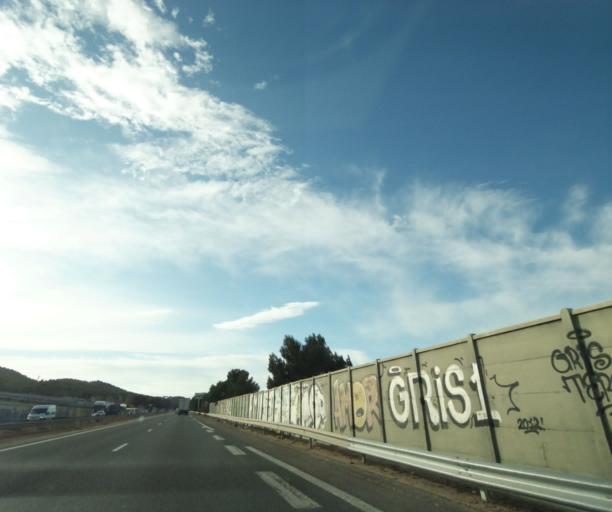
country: FR
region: Provence-Alpes-Cote d'Azur
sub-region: Departement des Bouches-du-Rhone
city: Martigues
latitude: 43.3999
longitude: 5.0965
